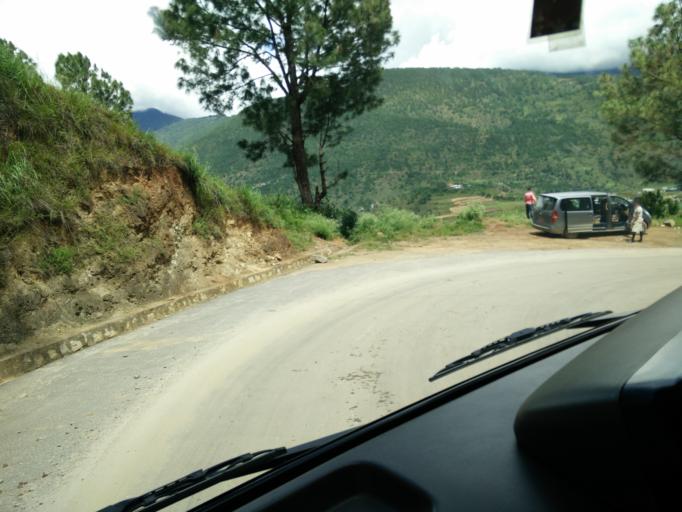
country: BT
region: Punakha
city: Pajo
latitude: 27.5225
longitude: 89.8665
